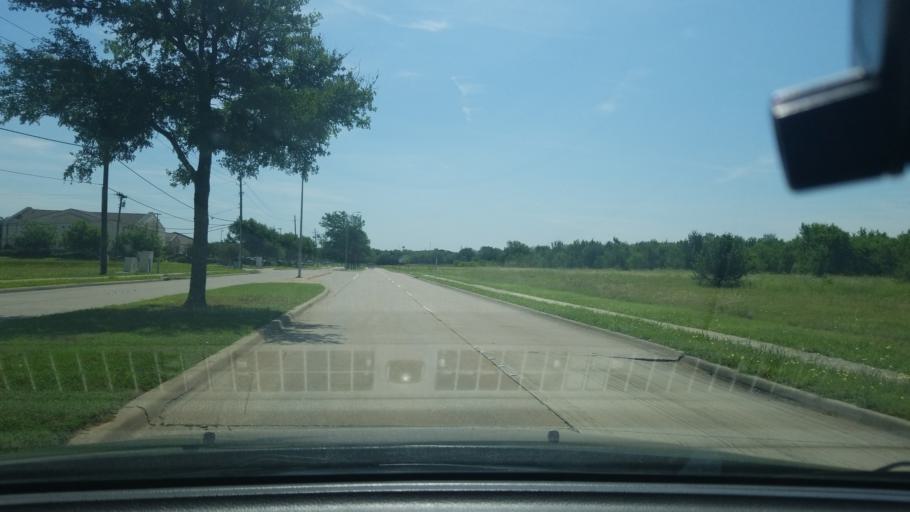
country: US
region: Texas
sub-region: Dallas County
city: Mesquite
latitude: 32.7703
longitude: -96.5812
